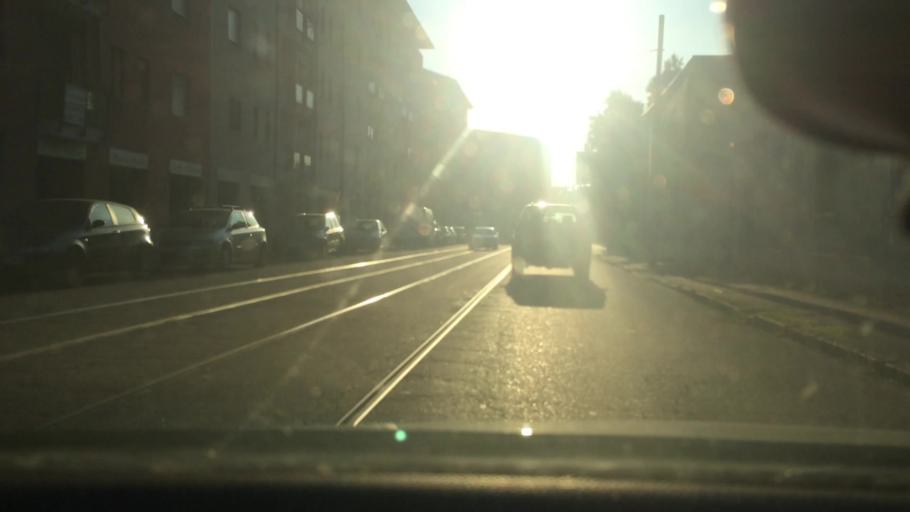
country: IT
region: Lombardy
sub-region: Citta metropolitana di Milano
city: Novate Milanese
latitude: 45.5086
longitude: 9.1346
